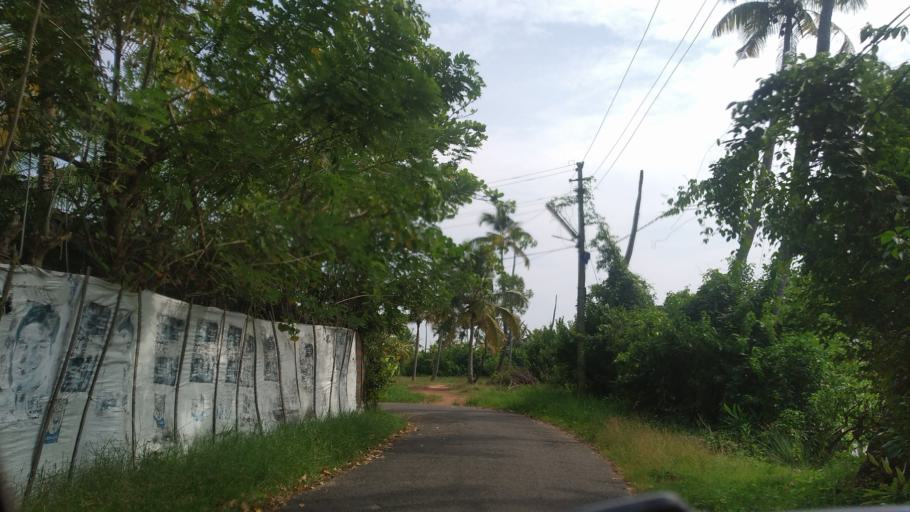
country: IN
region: Kerala
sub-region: Ernakulam
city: Elur
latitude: 10.0859
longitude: 76.1966
